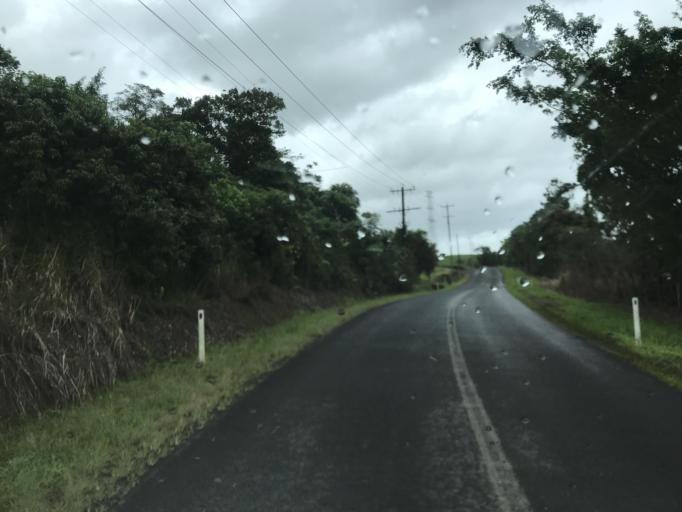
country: AU
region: Queensland
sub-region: Cassowary Coast
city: Innisfail
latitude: -17.5160
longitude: 145.9751
